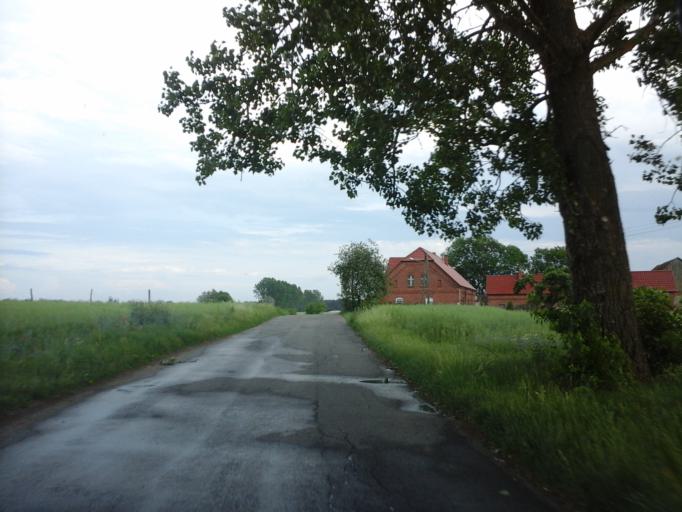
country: PL
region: West Pomeranian Voivodeship
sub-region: Powiat choszczenski
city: Recz
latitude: 53.2085
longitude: 15.5510
